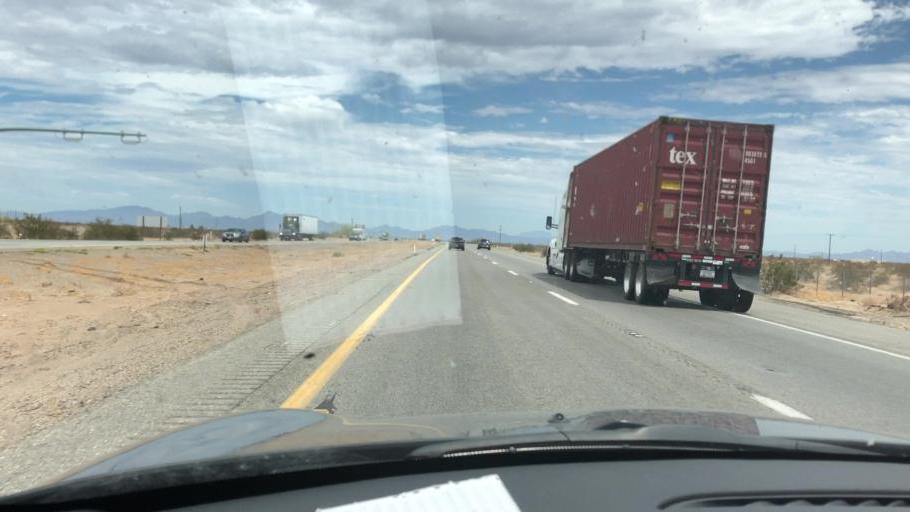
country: US
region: California
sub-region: Riverside County
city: Mesa Verde
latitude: 33.6083
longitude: -114.7194
